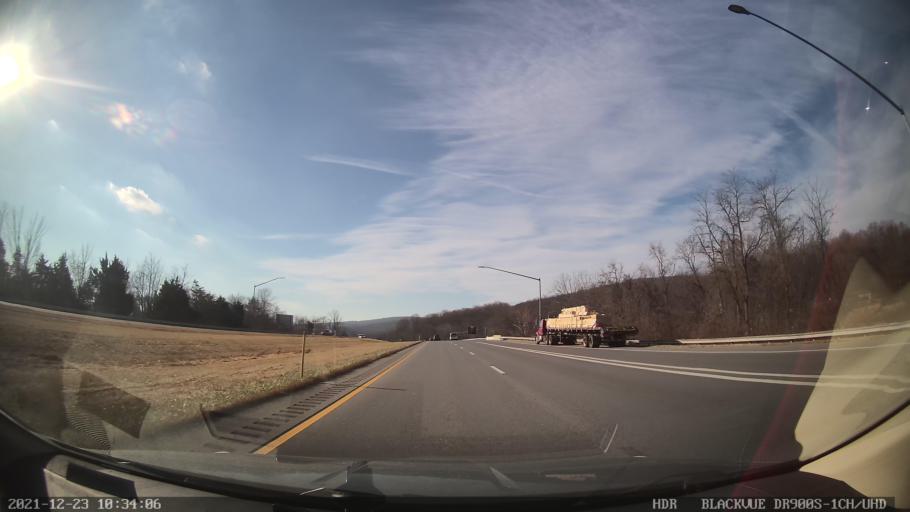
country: US
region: Maryland
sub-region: Frederick County
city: Thurmont
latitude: 39.6338
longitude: -77.4138
